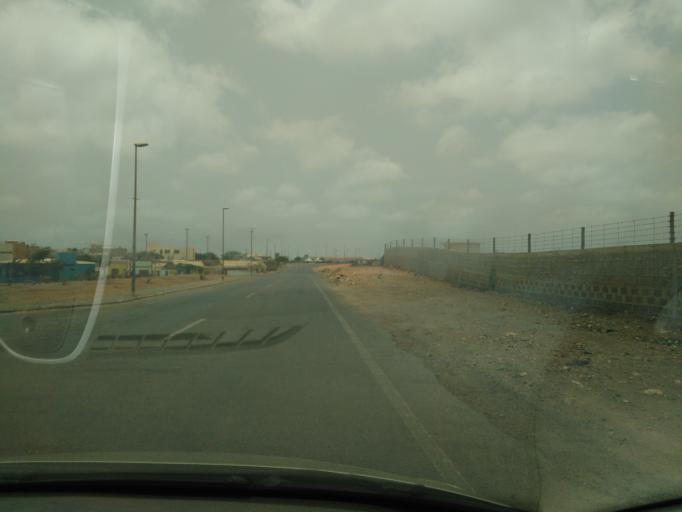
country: CV
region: Sal
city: Espargos
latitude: 16.7546
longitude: -22.9487
